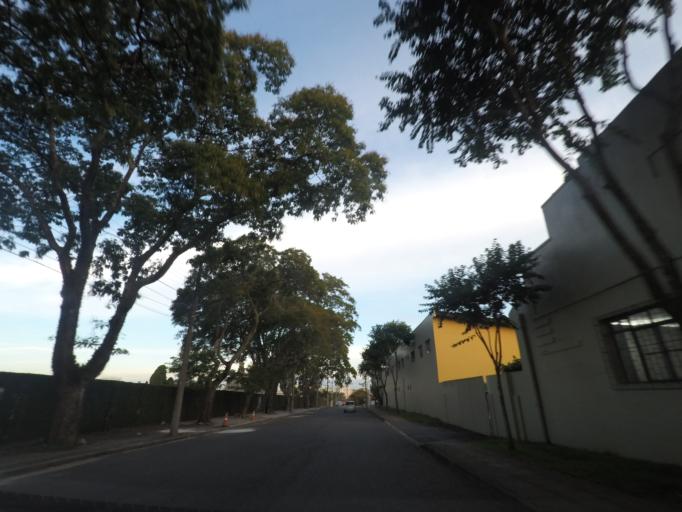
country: BR
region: Parana
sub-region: Curitiba
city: Curitiba
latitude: -25.4192
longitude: -49.2778
